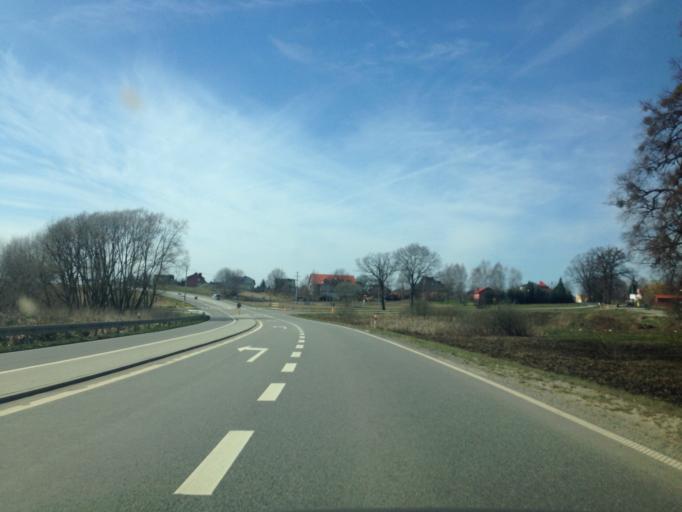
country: PL
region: Pomeranian Voivodeship
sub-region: Powiat starogardzki
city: Smetowo Graniczne
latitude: 53.7410
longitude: 18.6958
